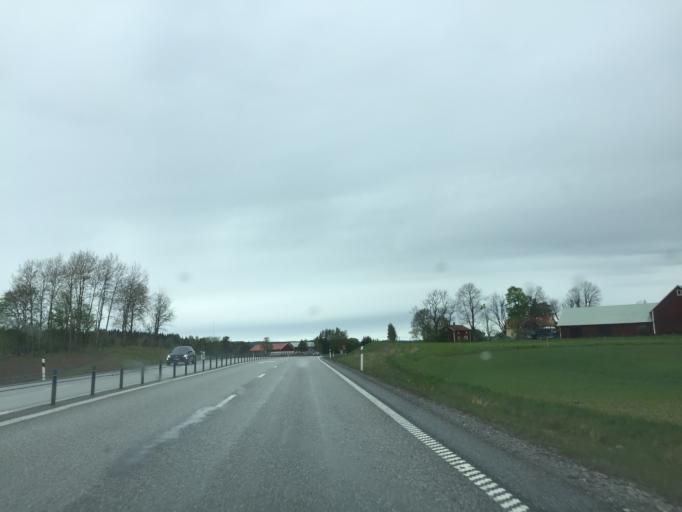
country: SE
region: OErebro
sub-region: Orebro Kommun
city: Hovsta
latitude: 59.4009
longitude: 15.1923
